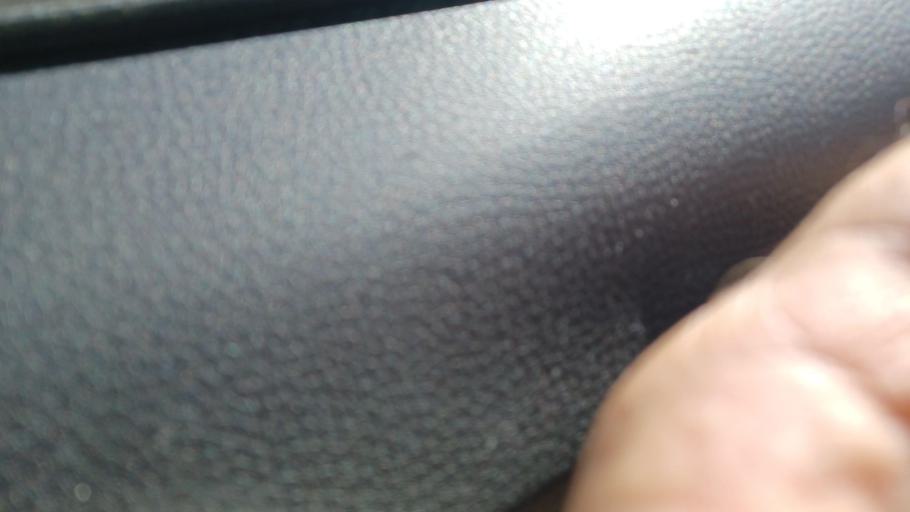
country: CY
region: Pafos
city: Pegeia
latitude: 34.8961
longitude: 32.4241
